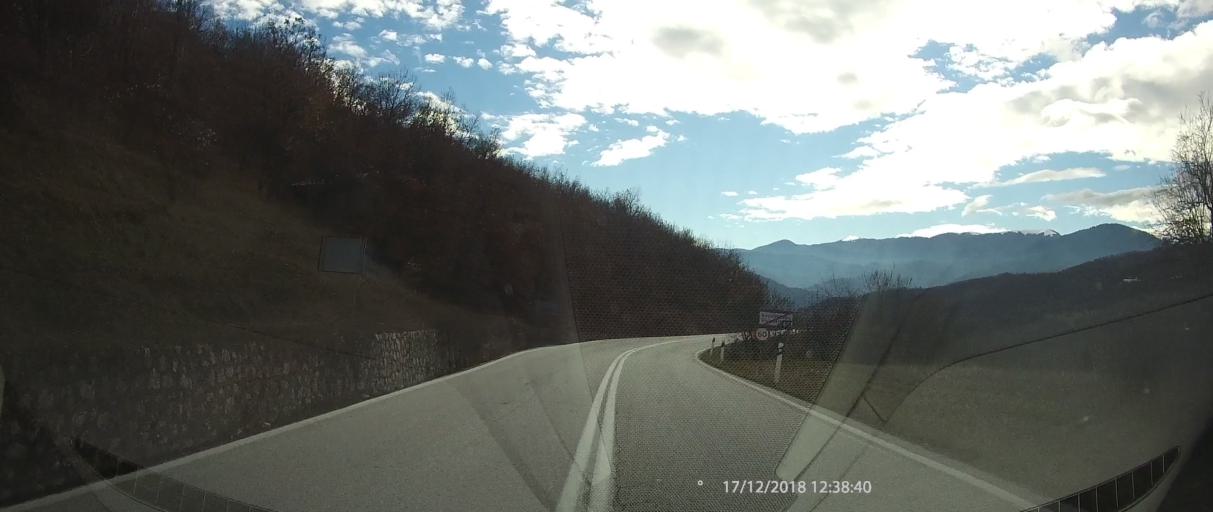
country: GR
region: Epirus
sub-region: Nomos Ioanninon
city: Metsovo
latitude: 39.8072
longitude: 21.3487
